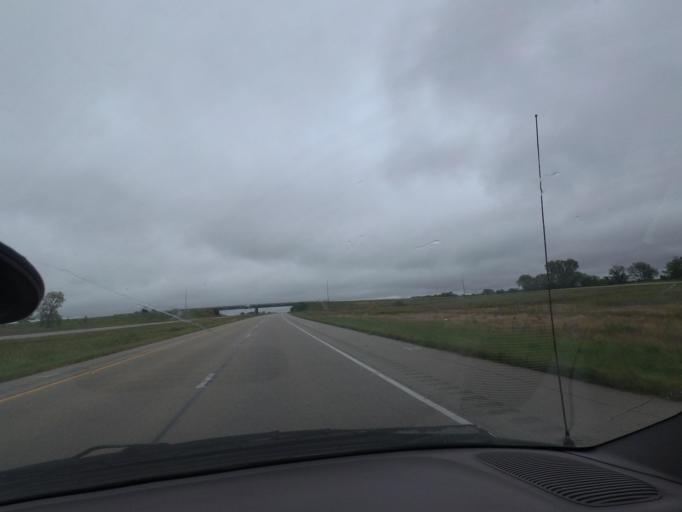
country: US
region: Illinois
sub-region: Sangamon County
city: Riverton
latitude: 39.8376
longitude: -89.5238
